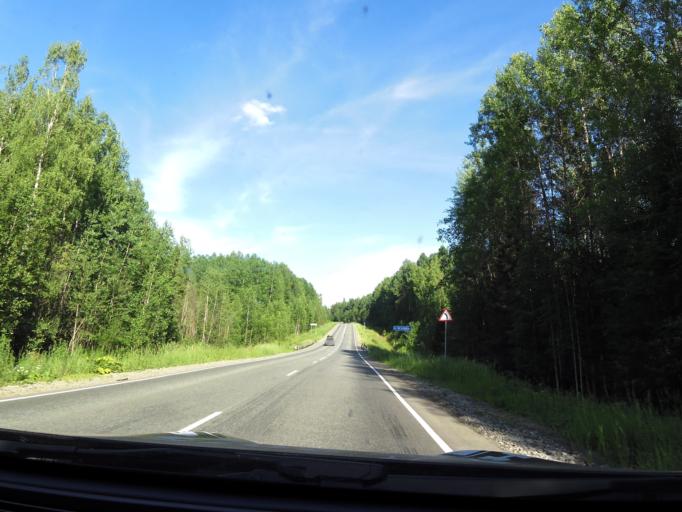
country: RU
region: Kirov
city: Chernaya Kholunitsa
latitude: 58.8595
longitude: 51.6226
